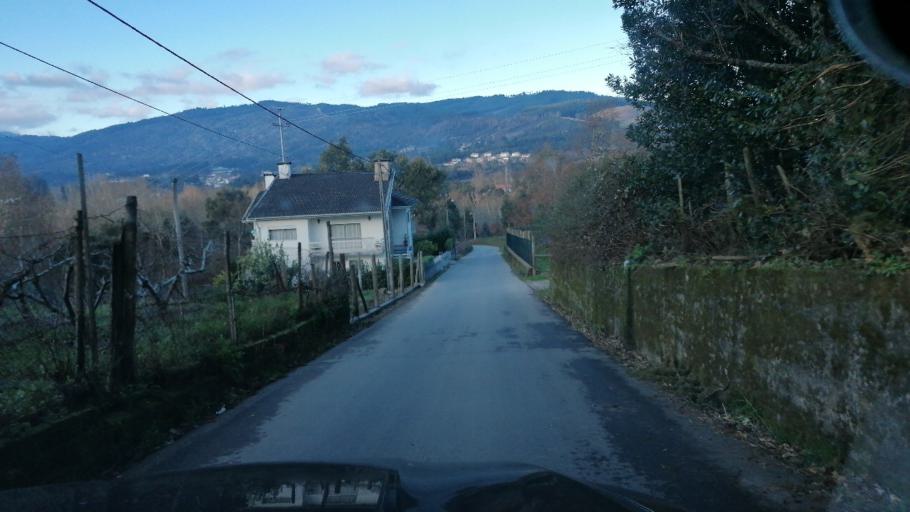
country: PT
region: Vila Real
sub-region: Mondim de Basto
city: Mondim de Basto
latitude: 41.4252
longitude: -7.9857
